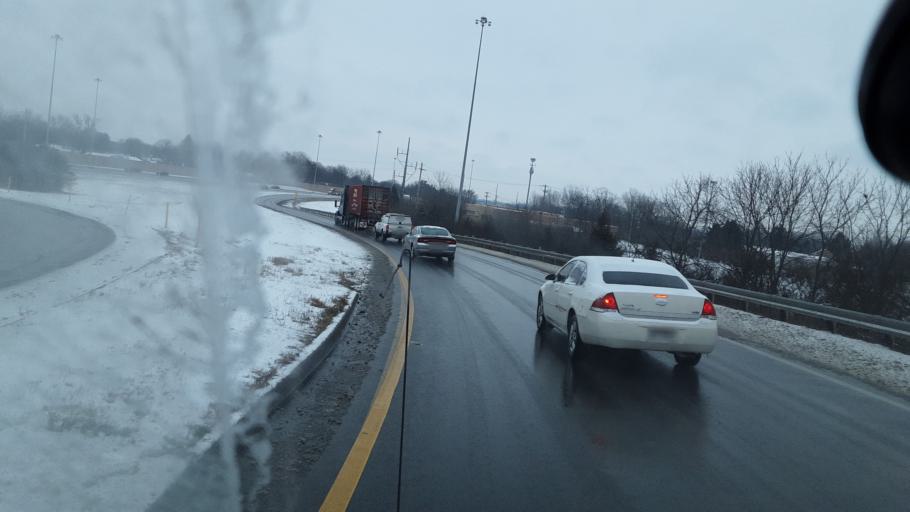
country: US
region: Ohio
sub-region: Franklin County
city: Bexley
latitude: 39.9308
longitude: -82.9143
